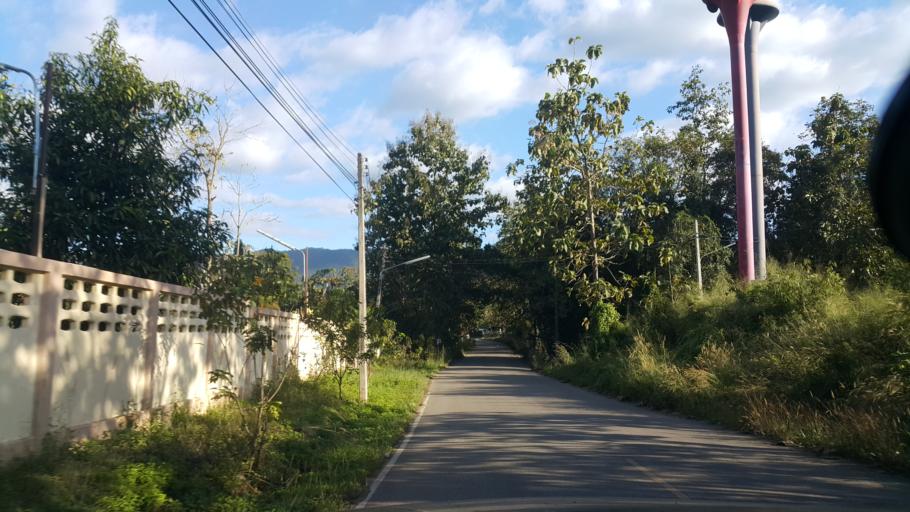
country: TH
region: Chiang Mai
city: Mae On
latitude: 18.7720
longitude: 99.2508
